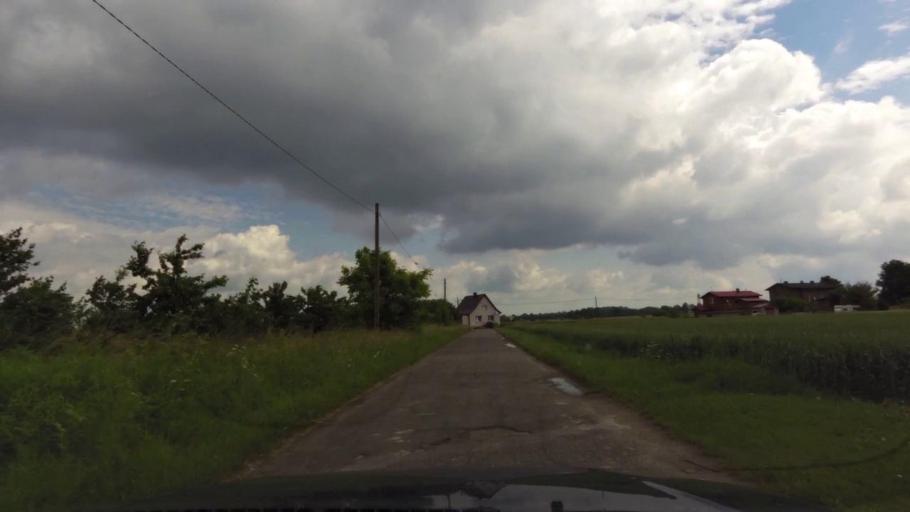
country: PL
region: West Pomeranian Voivodeship
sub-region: Powiat pyrzycki
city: Lipiany
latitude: 52.9630
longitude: 14.9583
